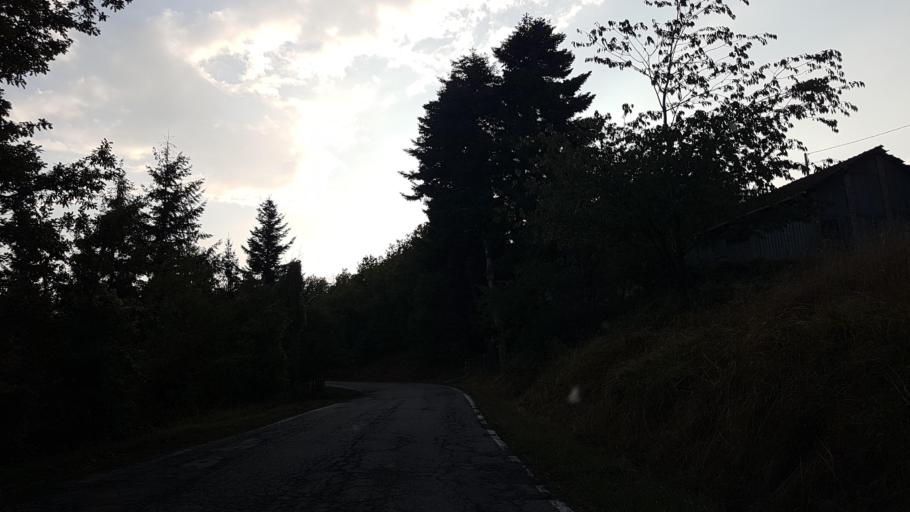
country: IT
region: Emilia-Romagna
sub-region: Provincia di Parma
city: Tornolo
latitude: 44.4523
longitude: 9.6492
